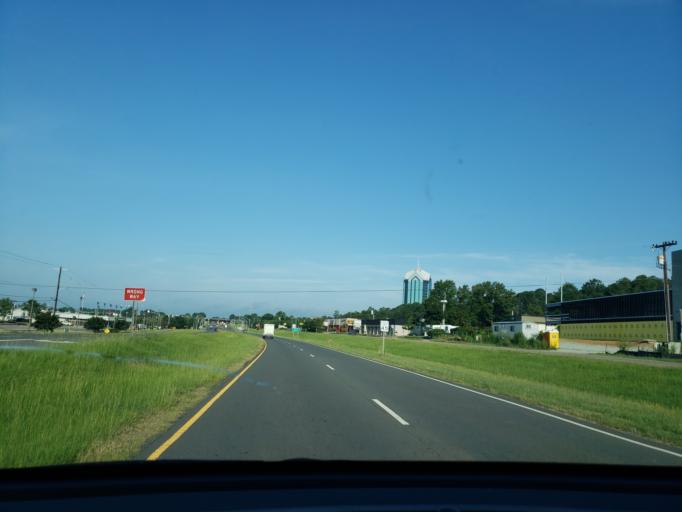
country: US
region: North Carolina
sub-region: Durham County
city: Durham
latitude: 35.9713
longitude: -78.9512
